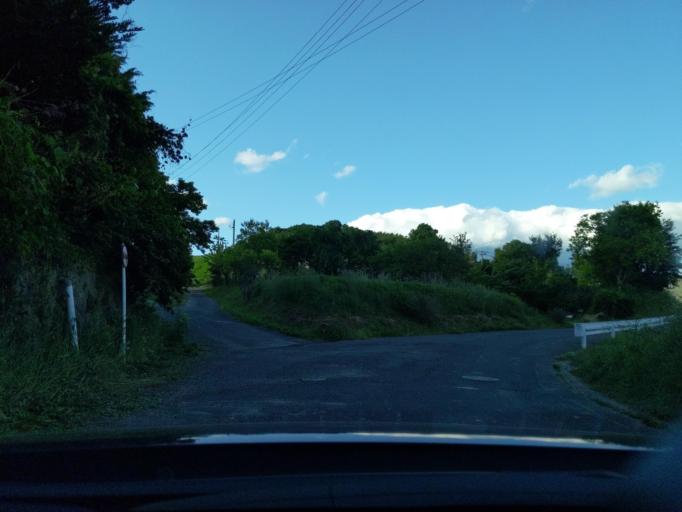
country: JP
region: Fukushima
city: Miharu
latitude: 37.4268
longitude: 140.4302
